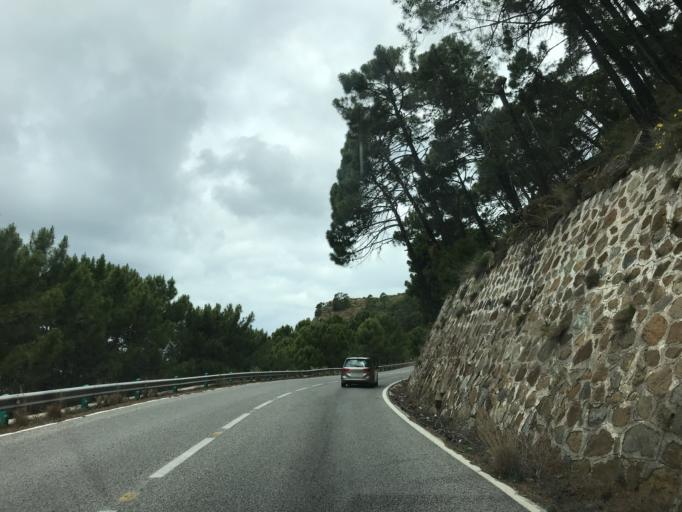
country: ES
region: Andalusia
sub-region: Provincia de Malaga
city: Benahavis
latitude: 36.5684
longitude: -5.0586
